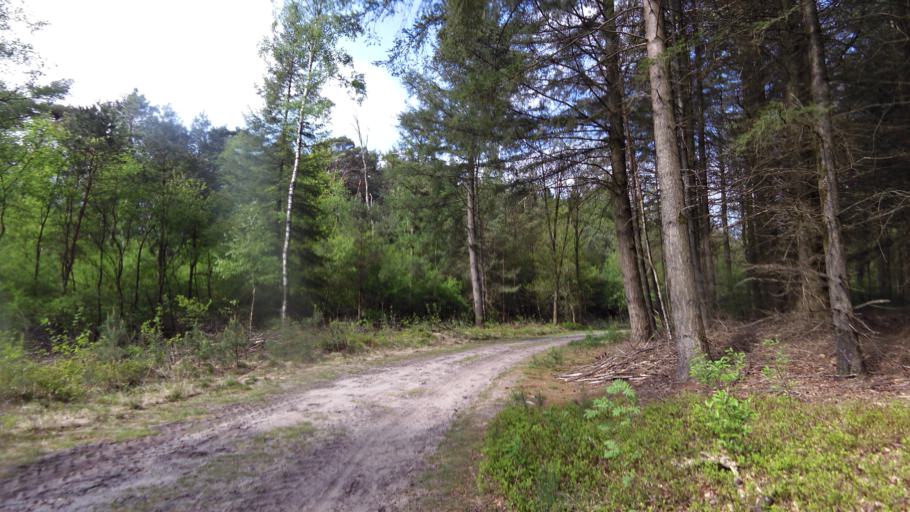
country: NL
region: Gelderland
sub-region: Gemeente Renkum
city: Heelsum
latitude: 52.0163
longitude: 5.7414
